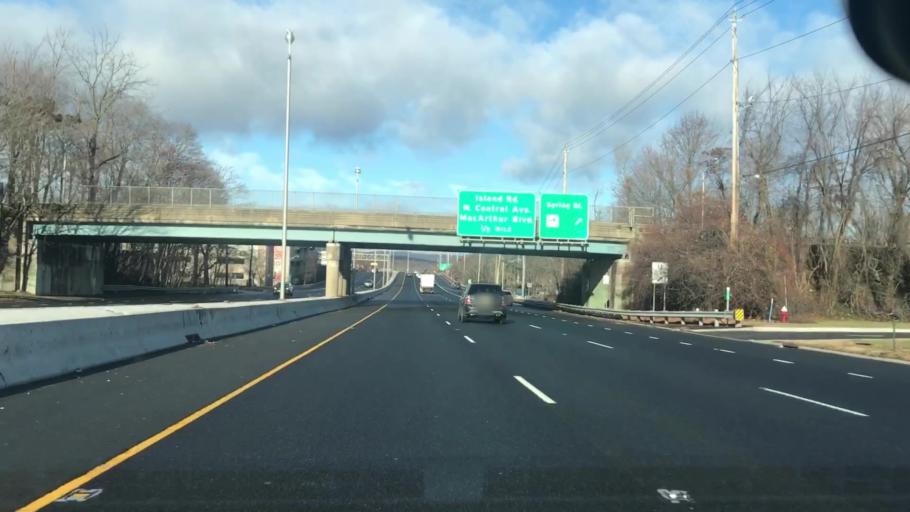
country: US
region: New Jersey
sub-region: Bergen County
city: Ramsey
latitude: 41.0728
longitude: -74.1415
